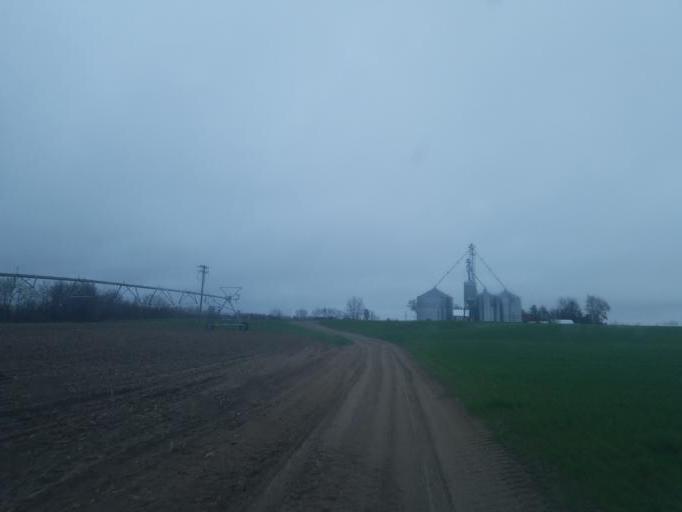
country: US
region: Michigan
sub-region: Montcalm County
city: Edmore
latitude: 43.4668
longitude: -85.0249
